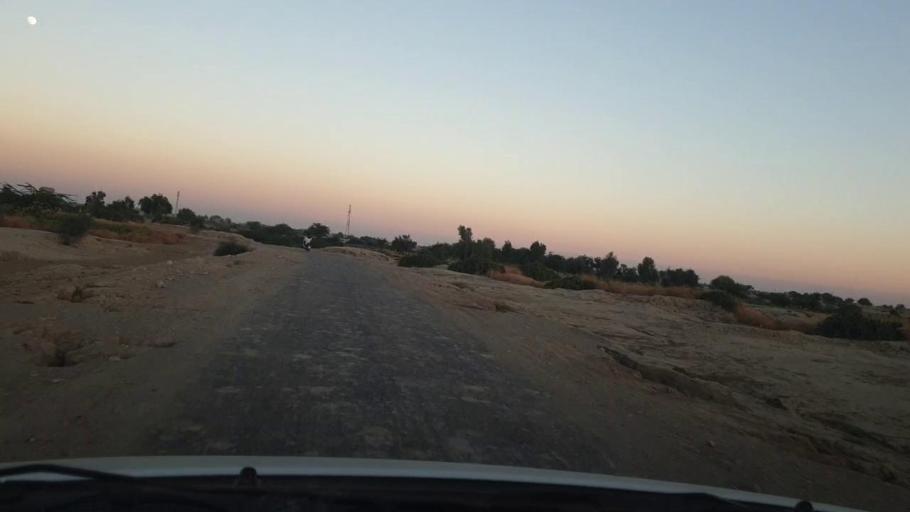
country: PK
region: Sindh
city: Johi
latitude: 26.8295
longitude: 67.4657
